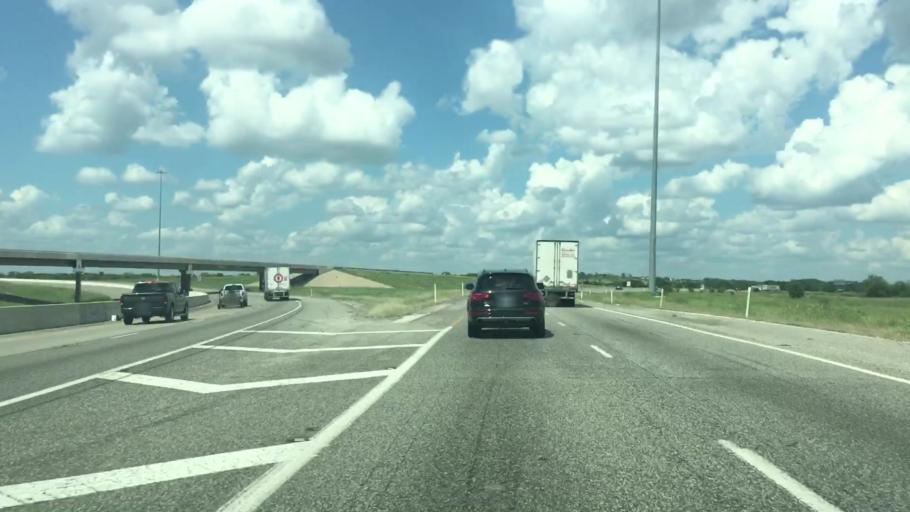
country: US
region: Texas
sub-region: Hill County
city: Hillsboro
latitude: 32.0536
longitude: -97.0933
